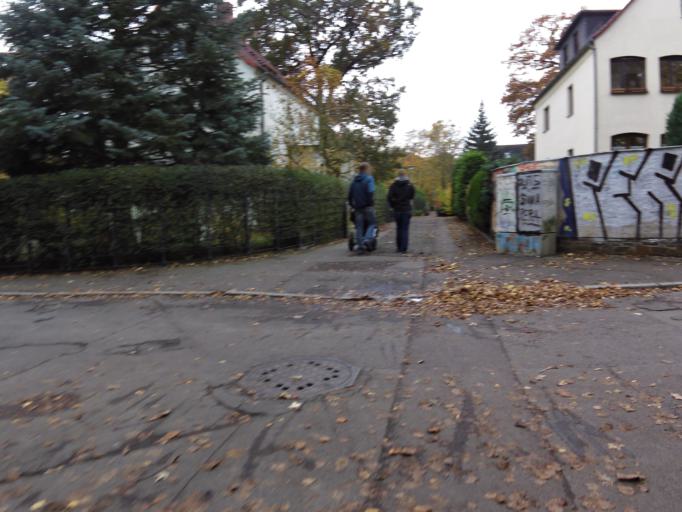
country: DE
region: Saxony
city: Leipzig
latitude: 51.3113
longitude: 12.3674
